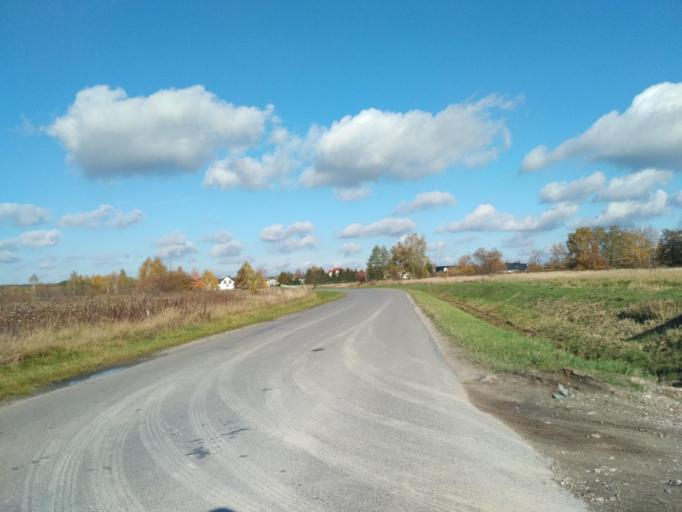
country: PL
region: Subcarpathian Voivodeship
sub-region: Powiat rzeszowski
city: Swilcza
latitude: 50.1289
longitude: 21.9028
